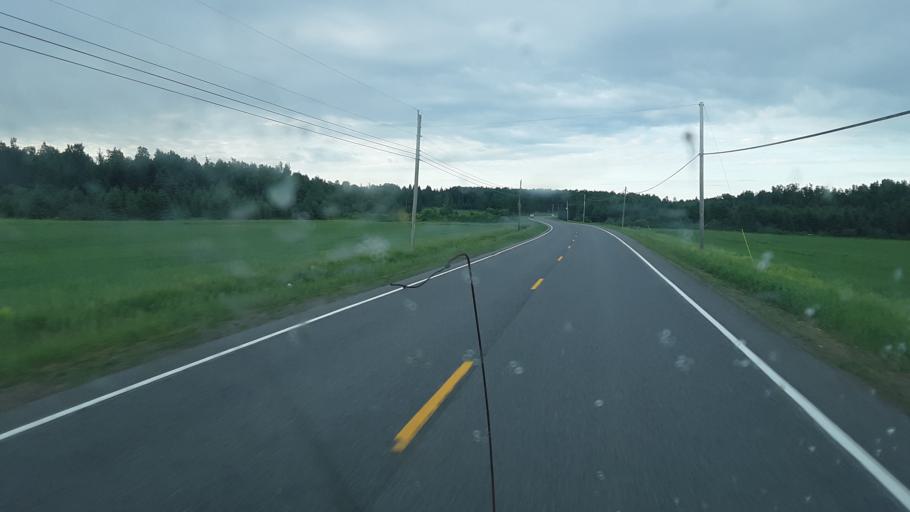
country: US
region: Maine
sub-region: Aroostook County
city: Presque Isle
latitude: 46.5175
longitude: -68.3561
